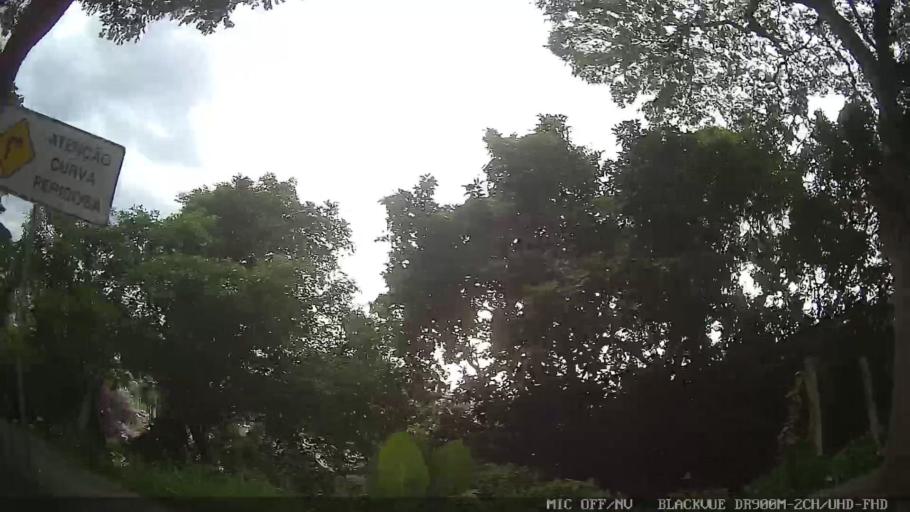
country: BR
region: Sao Paulo
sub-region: Atibaia
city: Atibaia
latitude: -23.1187
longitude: -46.5454
